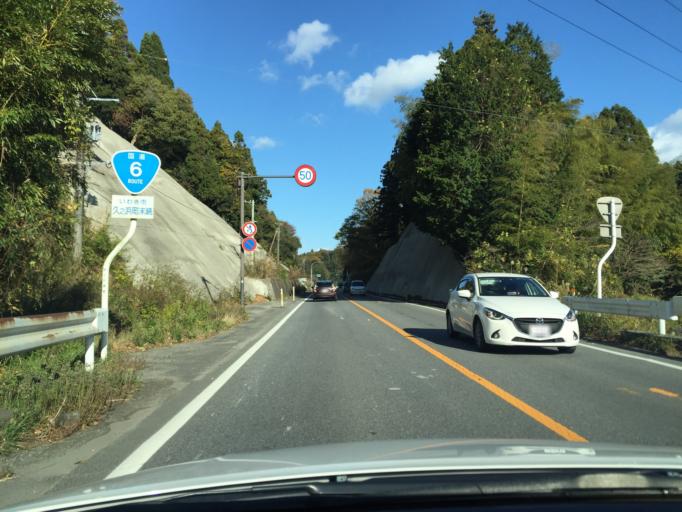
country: JP
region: Fukushima
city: Iwaki
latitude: 37.1712
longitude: 140.9940
